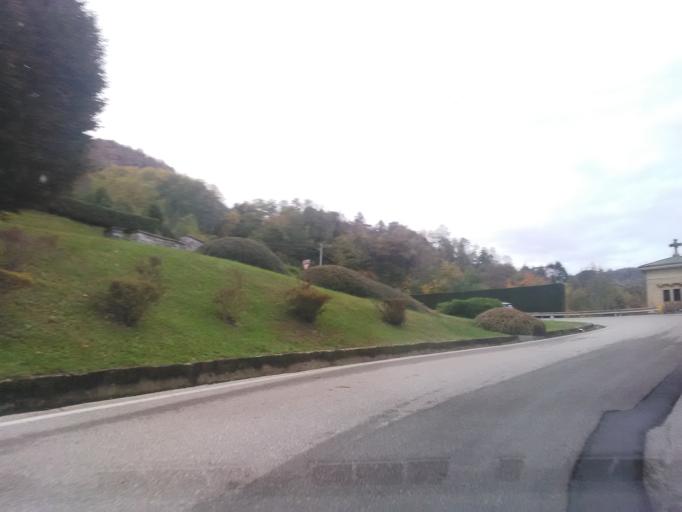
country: IT
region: Piedmont
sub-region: Provincia di Novara
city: Pella
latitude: 45.7933
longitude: 8.3824
